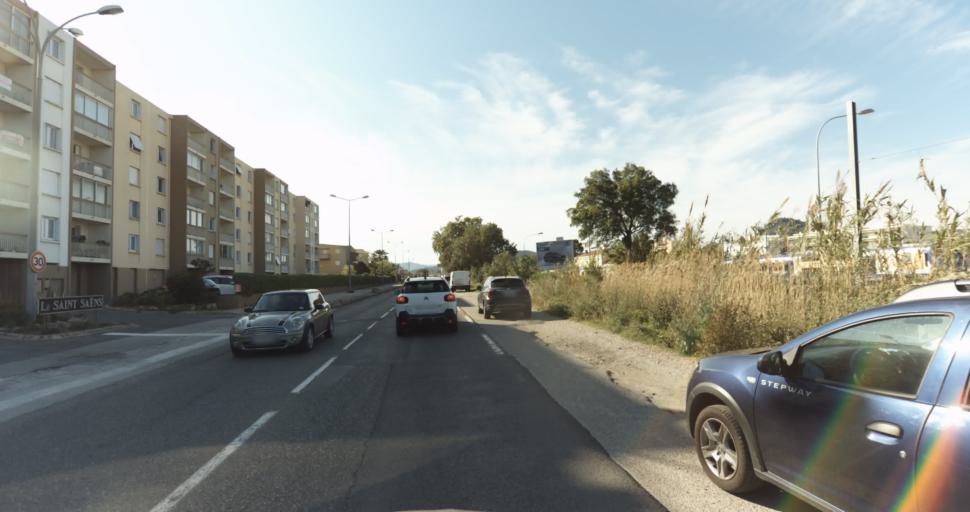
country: FR
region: Provence-Alpes-Cote d'Azur
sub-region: Departement du Var
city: Hyeres
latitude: 43.1073
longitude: 6.1251
